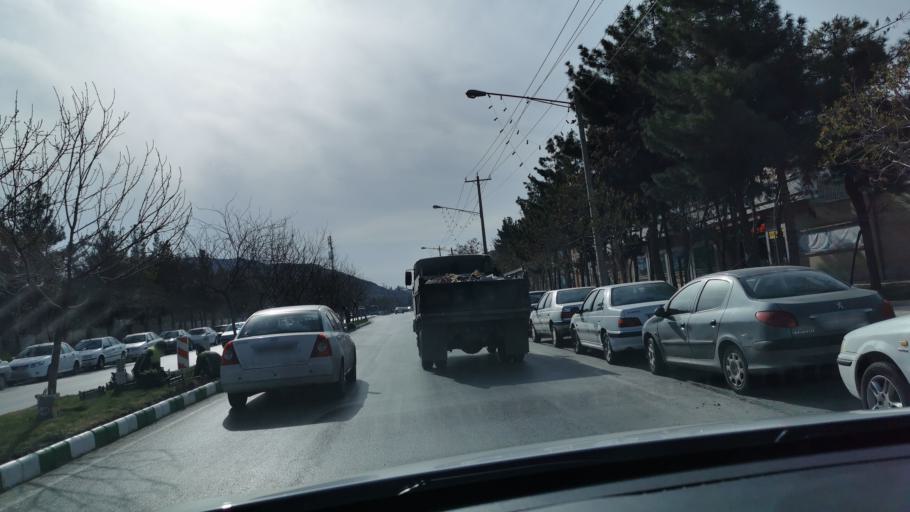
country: IR
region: Razavi Khorasan
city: Mashhad
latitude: 36.2820
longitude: 59.5522
